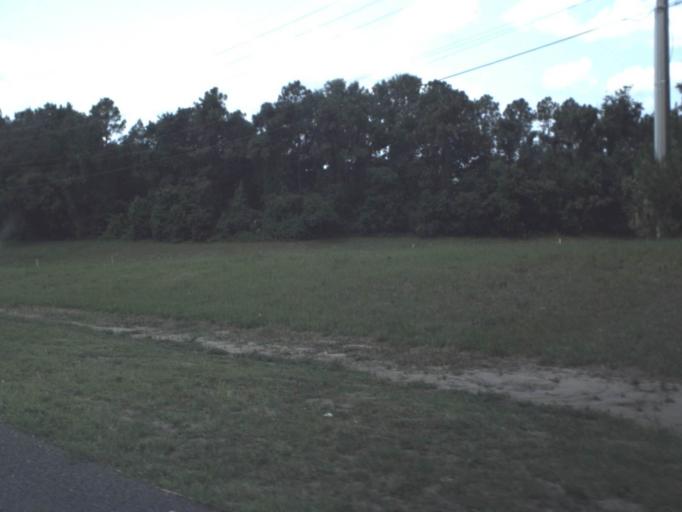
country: US
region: Florida
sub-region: Saint Johns County
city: Fruit Cove
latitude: 30.2013
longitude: -81.5519
